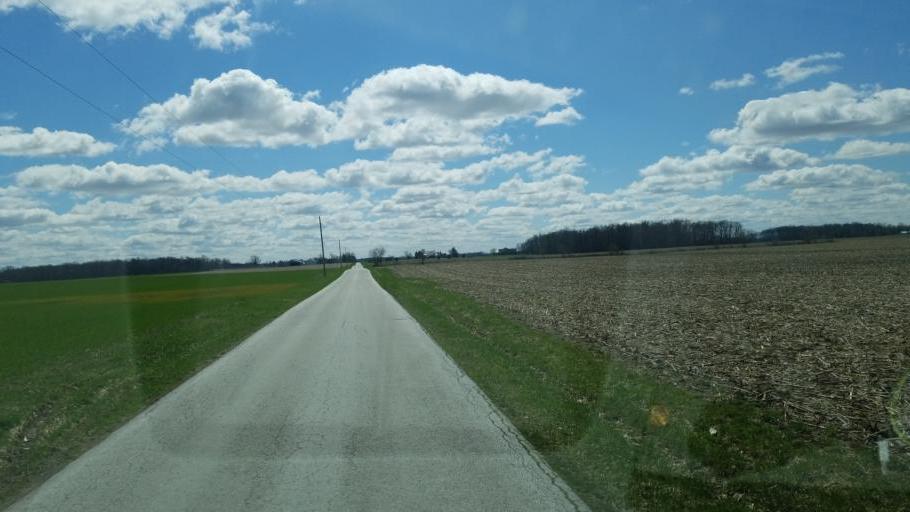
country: US
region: Ohio
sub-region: Hancock County
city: Arlington
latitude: 40.9299
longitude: -83.5368
